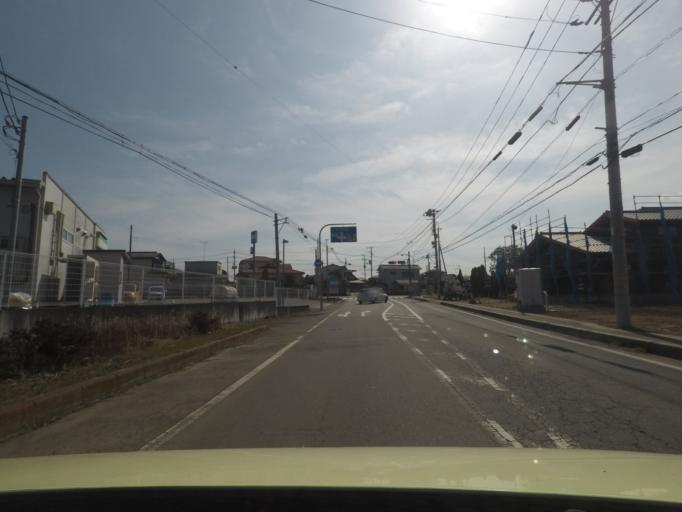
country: JP
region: Ibaraki
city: Ishioka
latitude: 36.1794
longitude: 140.3601
